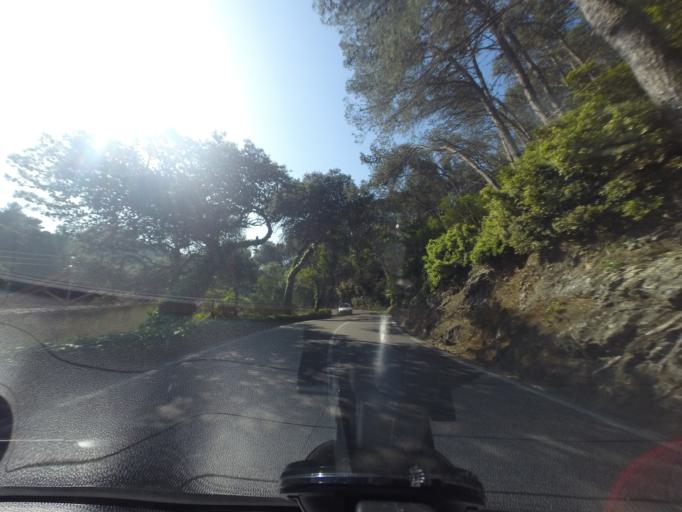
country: PT
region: Lisbon
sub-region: Cascais
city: Alcabideche
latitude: 38.7394
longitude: -9.4243
